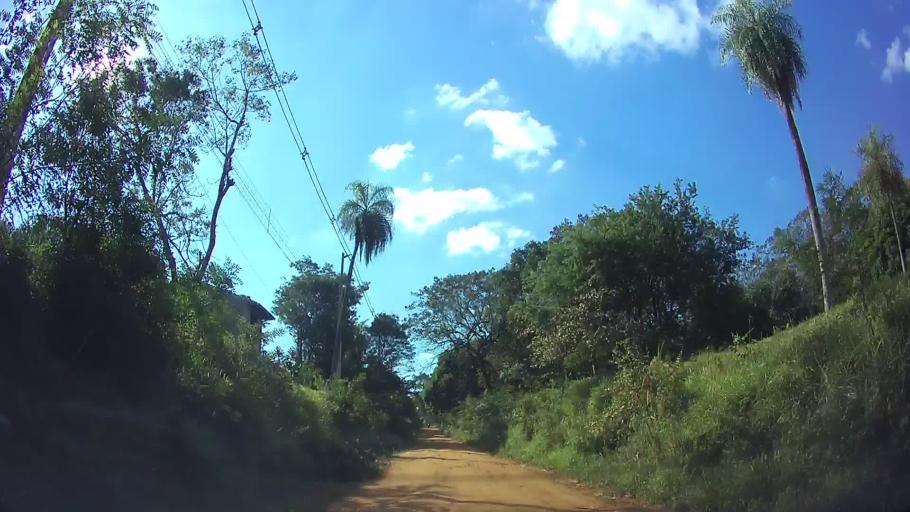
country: PY
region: Central
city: Limpio
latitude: -25.2519
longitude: -57.4748
